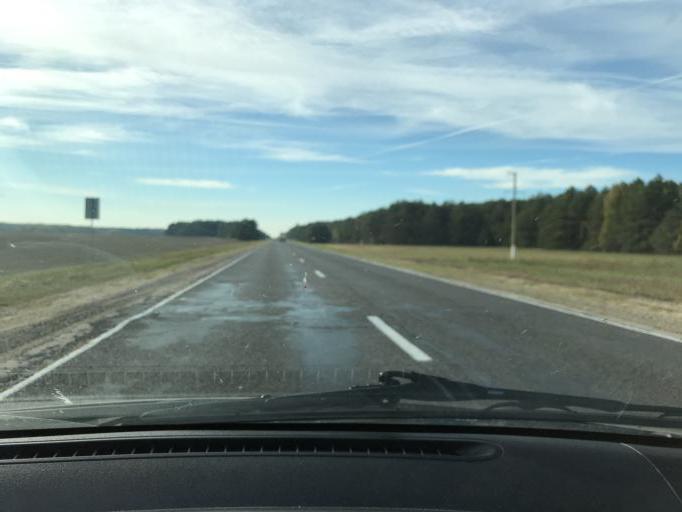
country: BY
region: Brest
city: Lahishyn
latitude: 52.1536
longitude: 25.8117
